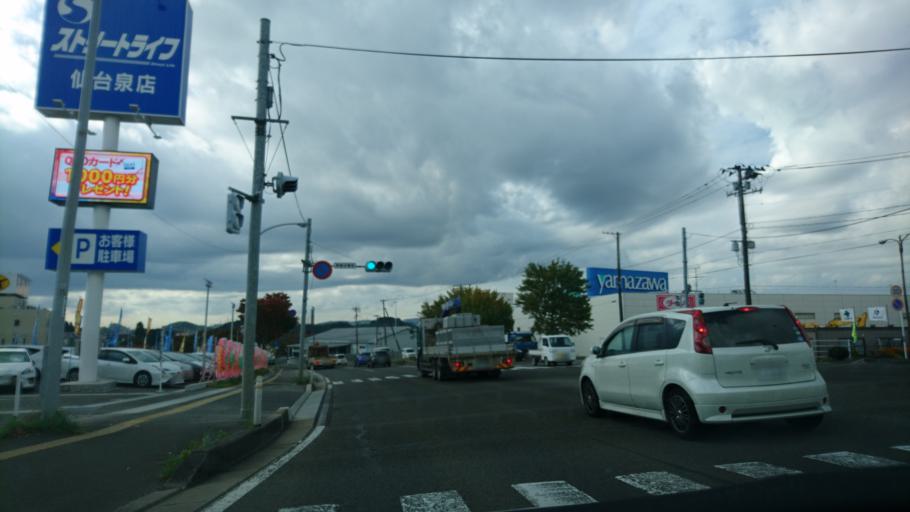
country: JP
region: Miyagi
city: Tomiya
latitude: 38.3568
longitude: 140.8712
